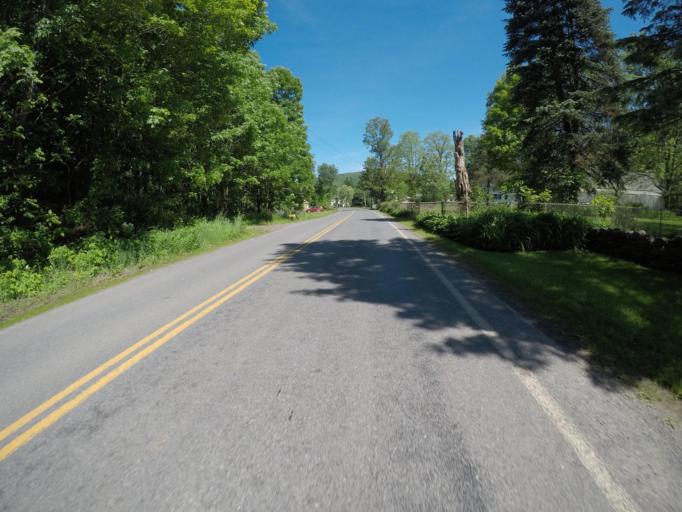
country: US
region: New York
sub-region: Delaware County
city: Delhi
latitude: 42.2035
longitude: -74.9696
